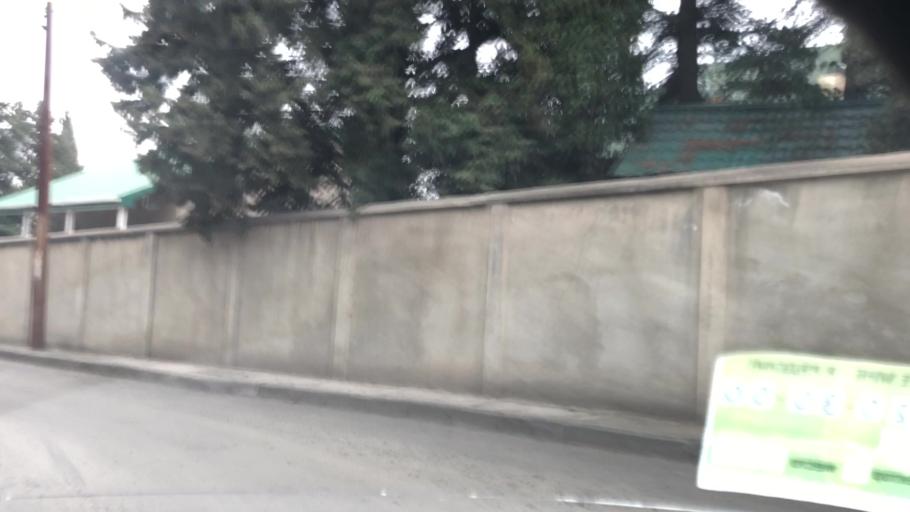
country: GE
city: Didi Lilo
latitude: 41.7030
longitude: 44.9278
